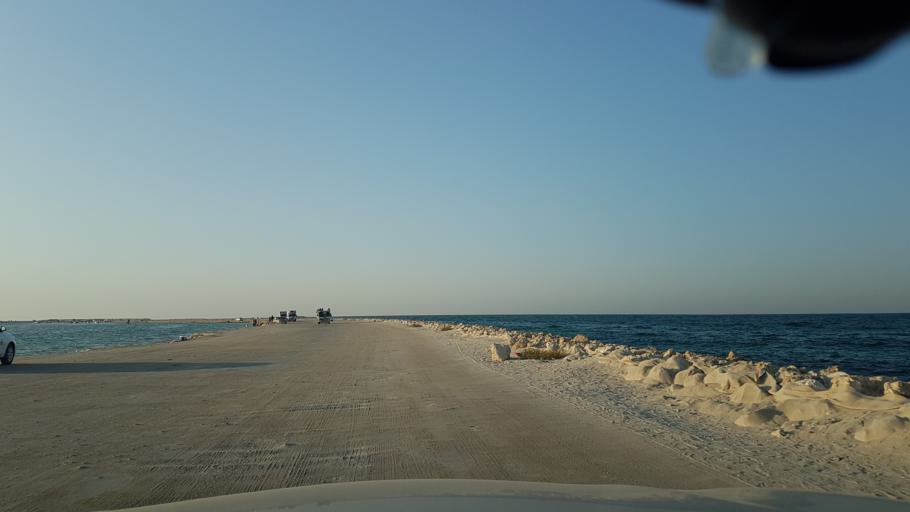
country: BH
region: Manama
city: Jidd Hafs
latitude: 26.2484
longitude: 50.5027
